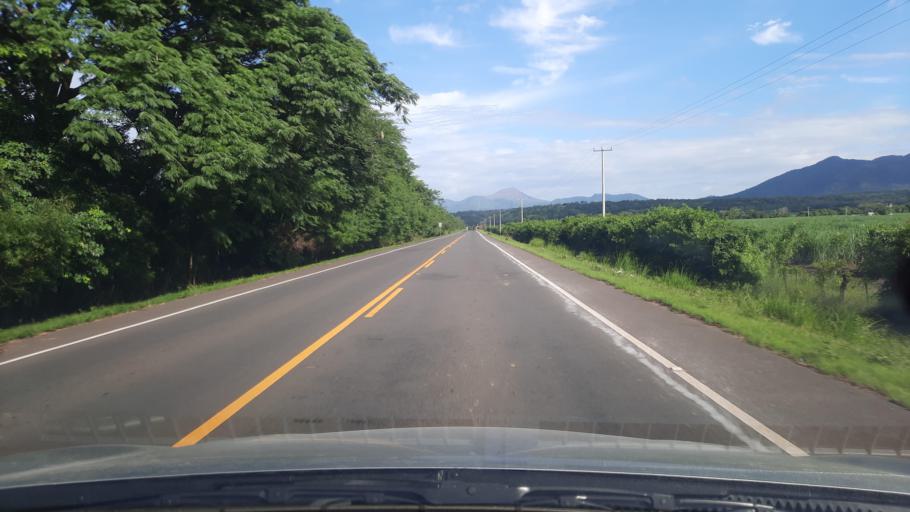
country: NI
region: Chinandega
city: Chichigalpa
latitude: 12.7525
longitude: -86.8964
